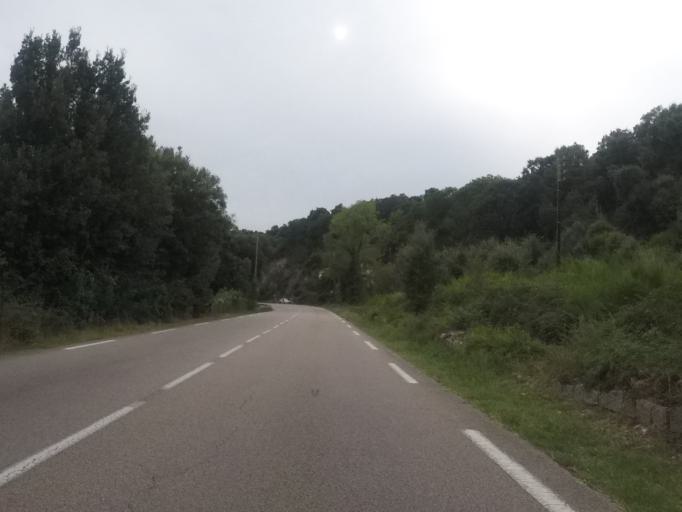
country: FR
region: Corsica
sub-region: Departement de la Corse-du-Sud
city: Peri
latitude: 42.0270
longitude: 8.9062
